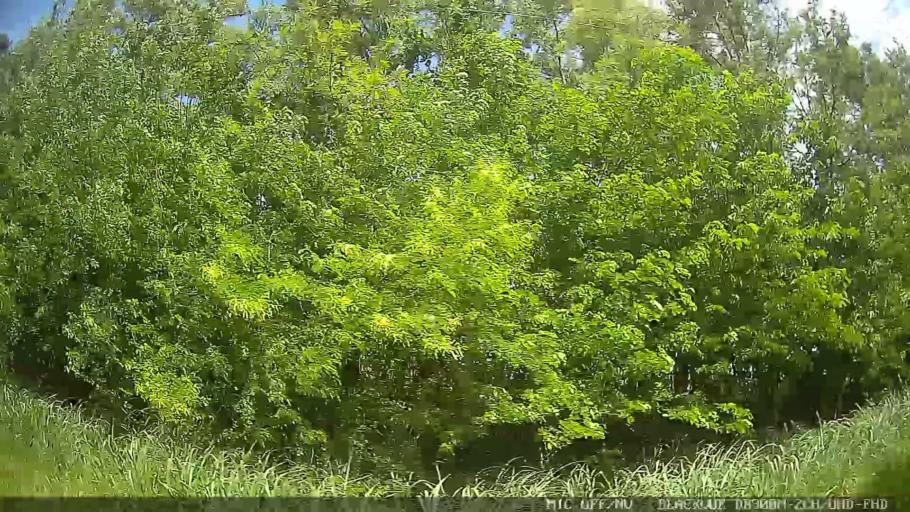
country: BR
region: Sao Paulo
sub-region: Conchas
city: Conchas
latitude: -23.0463
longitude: -48.0235
